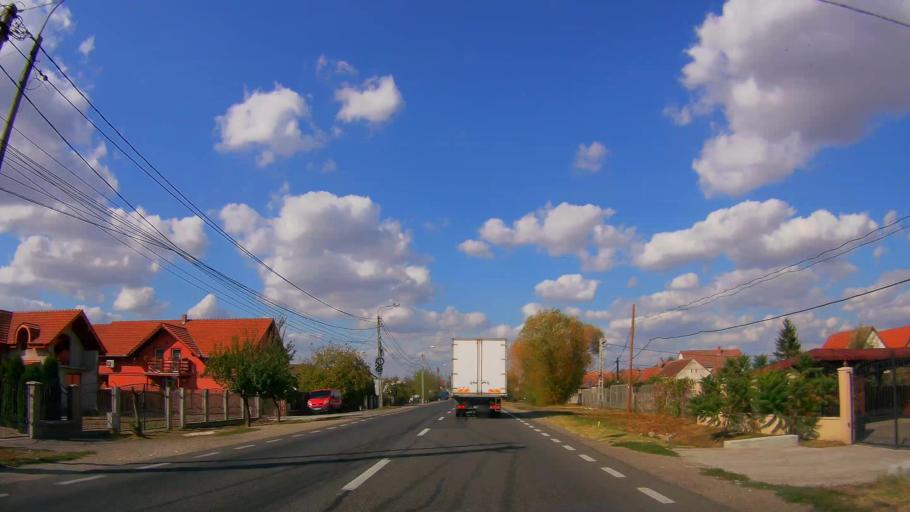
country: RO
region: Satu Mare
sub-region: Comuna Paulesti
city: Paulesti
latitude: 47.7402
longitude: 22.8827
